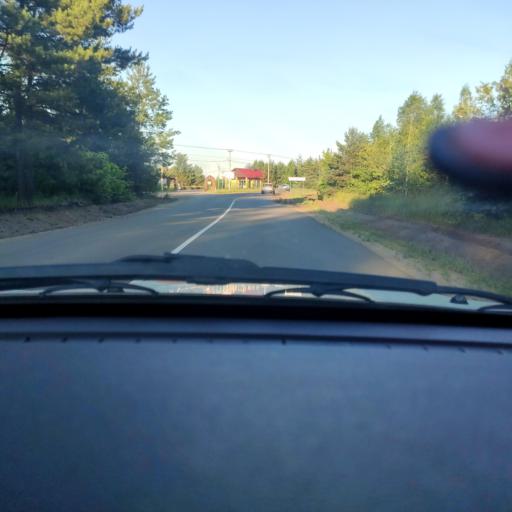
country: RU
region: Voronezj
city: Ramon'
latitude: 51.8923
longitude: 39.2413
